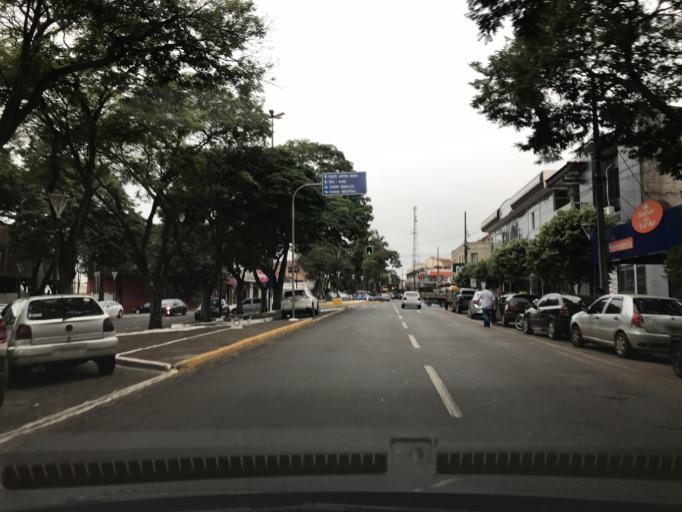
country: PY
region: Canindeyu
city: Salto del Guaira
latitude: -24.0821
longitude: -54.2499
